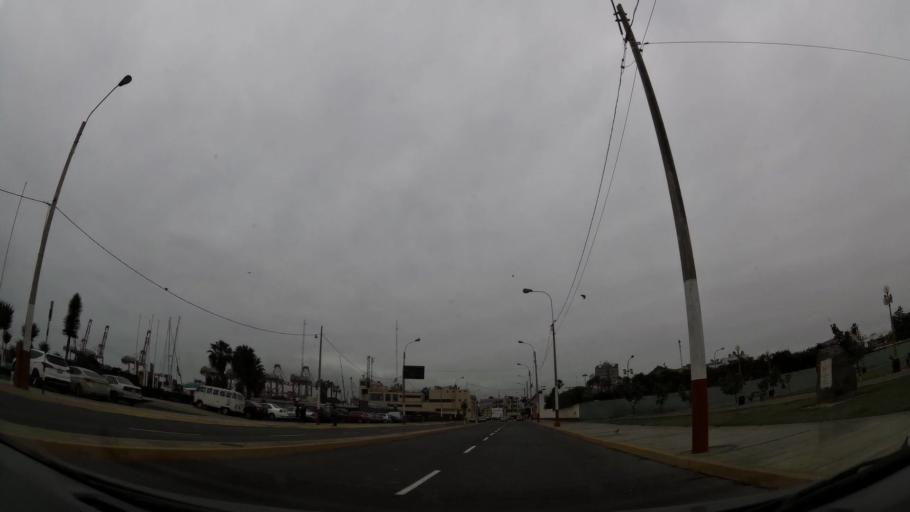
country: PE
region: Callao
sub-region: Callao
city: Callao
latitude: -12.0610
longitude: -77.1500
